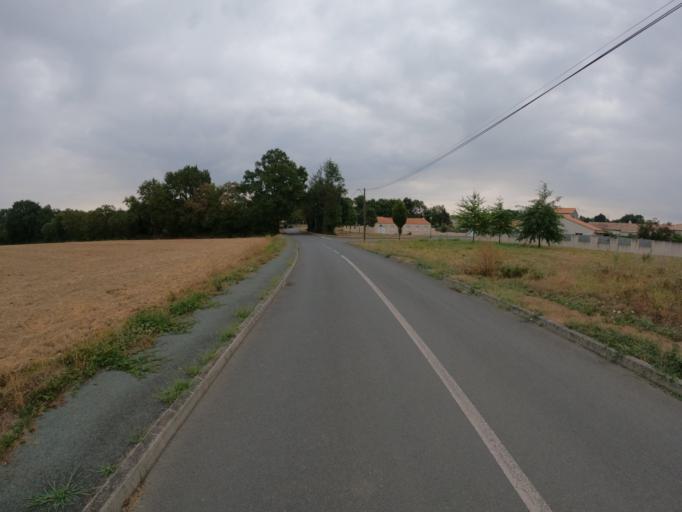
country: FR
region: Pays de la Loire
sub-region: Departement de la Vendee
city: La Guyonniere
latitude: 46.9683
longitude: -1.2569
